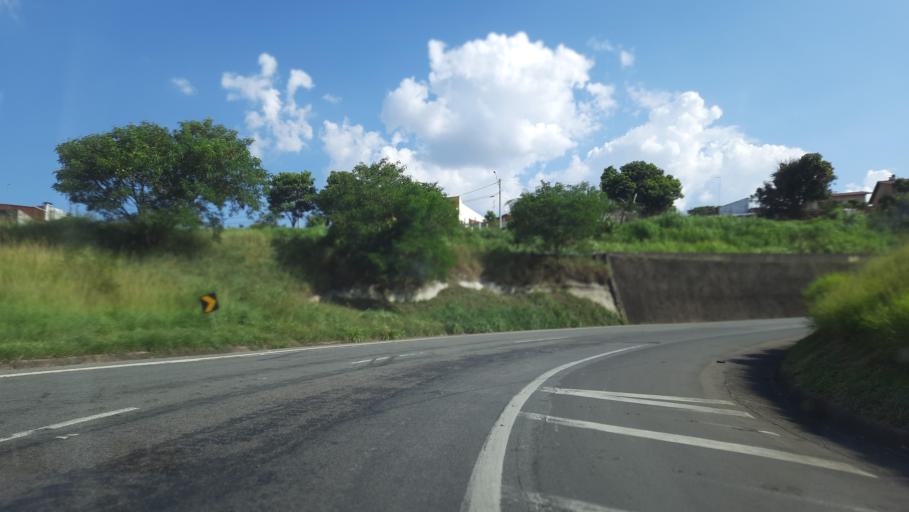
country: BR
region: Sao Paulo
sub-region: Campinas
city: Campinas
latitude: -22.8448
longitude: -47.0374
